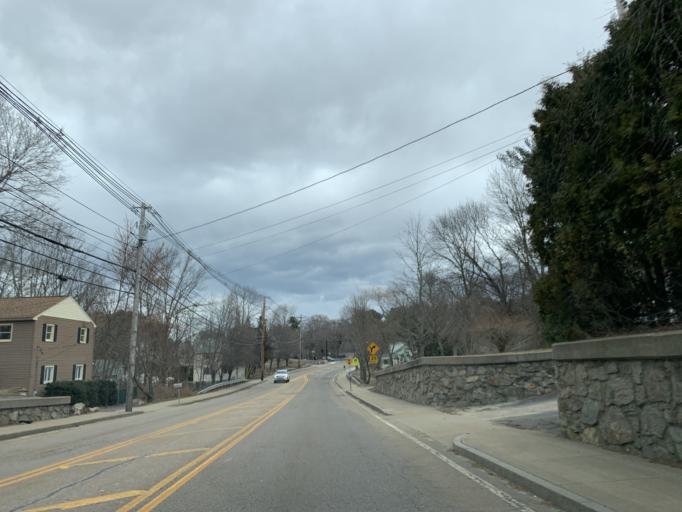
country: US
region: Massachusetts
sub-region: Norfolk County
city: Franklin
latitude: 42.0575
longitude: -71.4177
